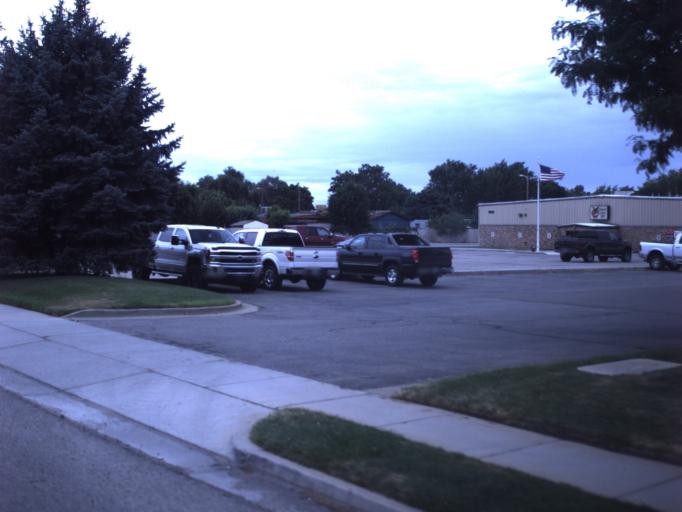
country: US
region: Utah
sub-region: Weber County
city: Ogden
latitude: 41.2476
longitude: -111.9783
